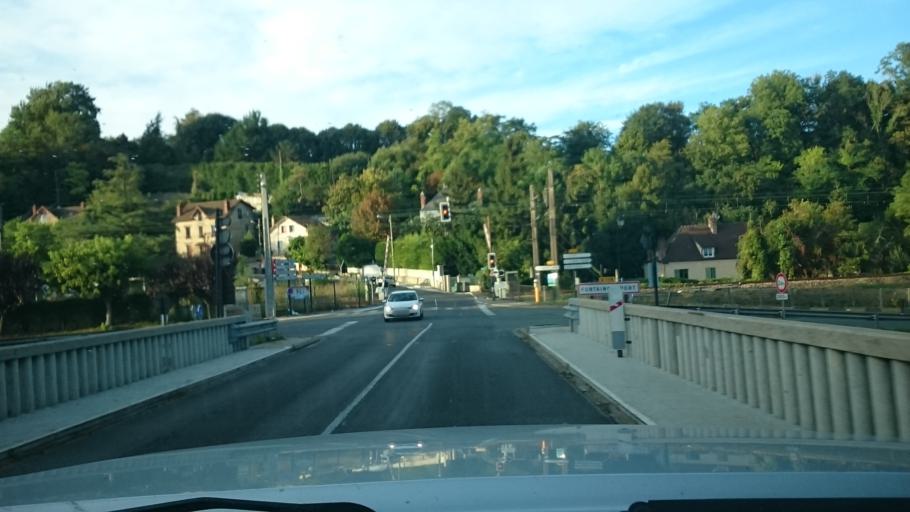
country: FR
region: Ile-de-France
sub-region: Departement de Seine-et-Marne
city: Samois-sur-Seine
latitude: 48.4863
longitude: 2.7525
